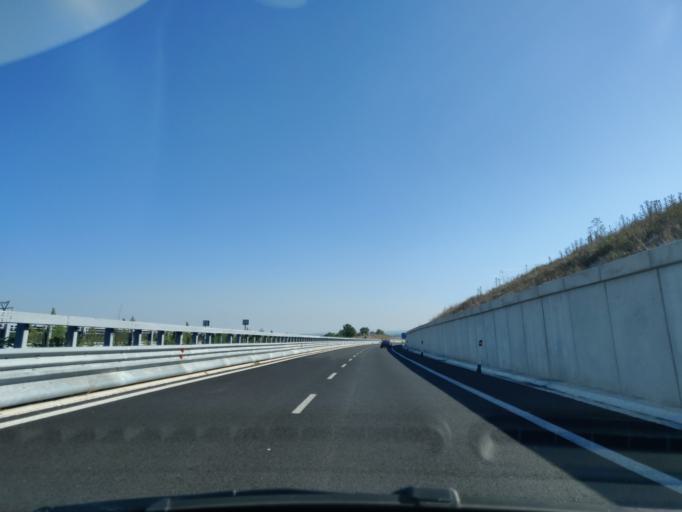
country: IT
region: Latium
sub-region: Provincia di Viterbo
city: Monte Romano
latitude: 42.2919
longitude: 11.9411
